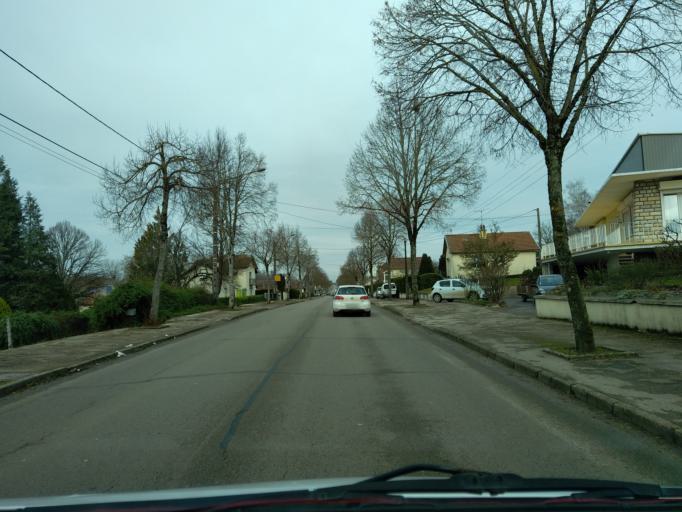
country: FR
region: Franche-Comte
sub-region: Departement de la Haute-Saone
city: Arc-les-Gray
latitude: 47.4643
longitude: 5.5830
